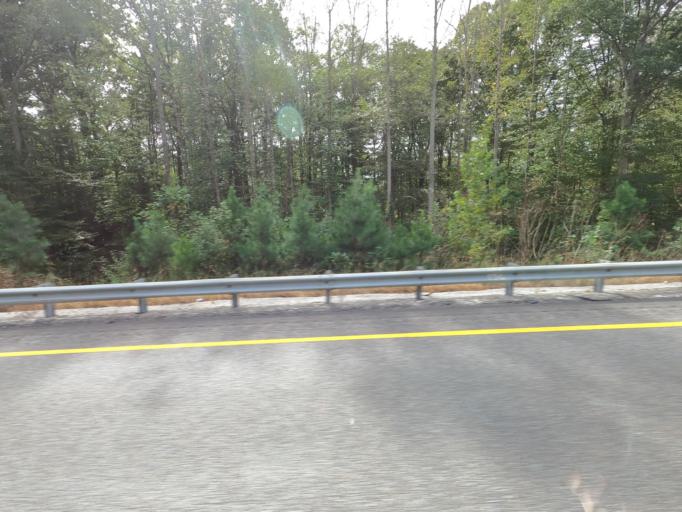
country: US
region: Tennessee
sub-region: Decatur County
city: Parsons
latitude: 35.8160
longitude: -88.2217
